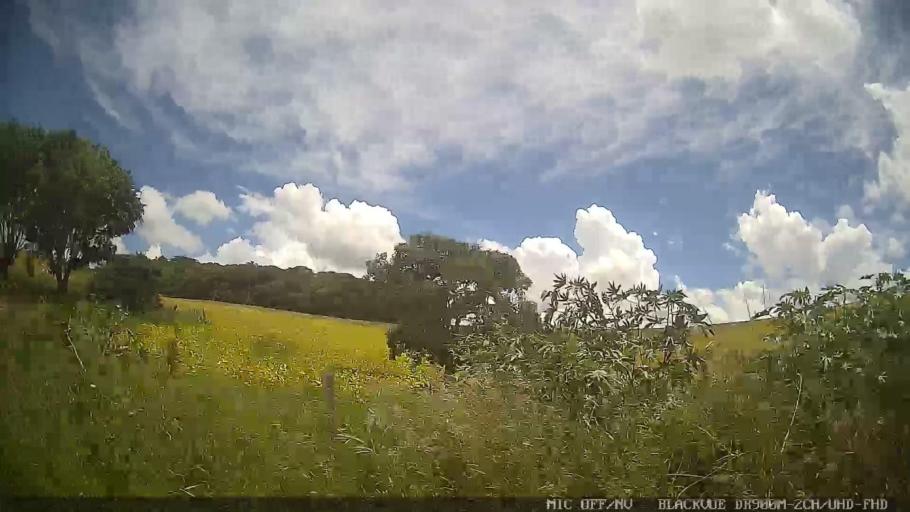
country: BR
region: Minas Gerais
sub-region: Extrema
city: Extrema
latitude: -22.7253
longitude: -46.4007
